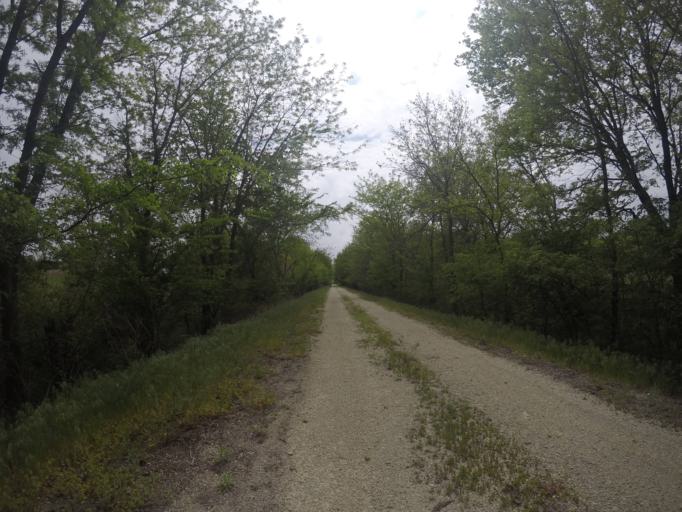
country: US
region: Nebraska
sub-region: Gage County
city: Wymore
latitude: 40.0302
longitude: -96.5794
